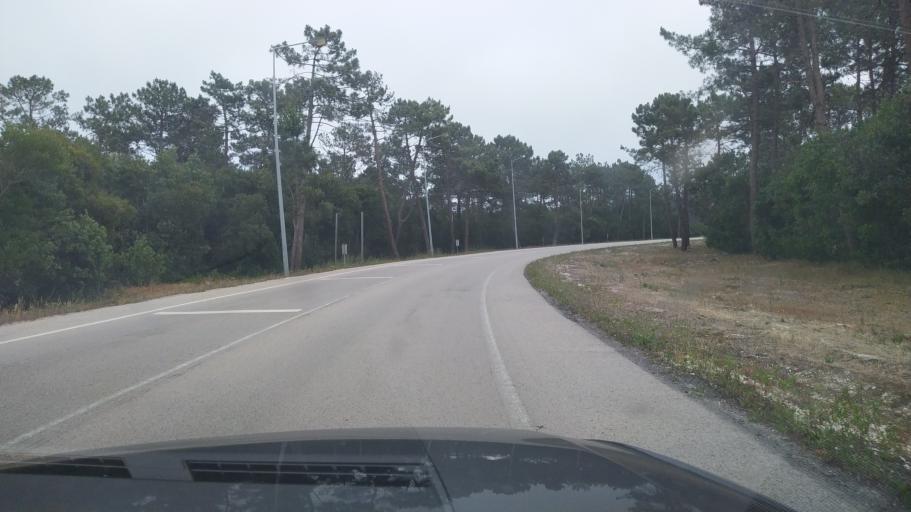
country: PT
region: Aveiro
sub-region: Ilhavo
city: Gafanha da Nazare
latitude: 40.6201
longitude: -8.7155
